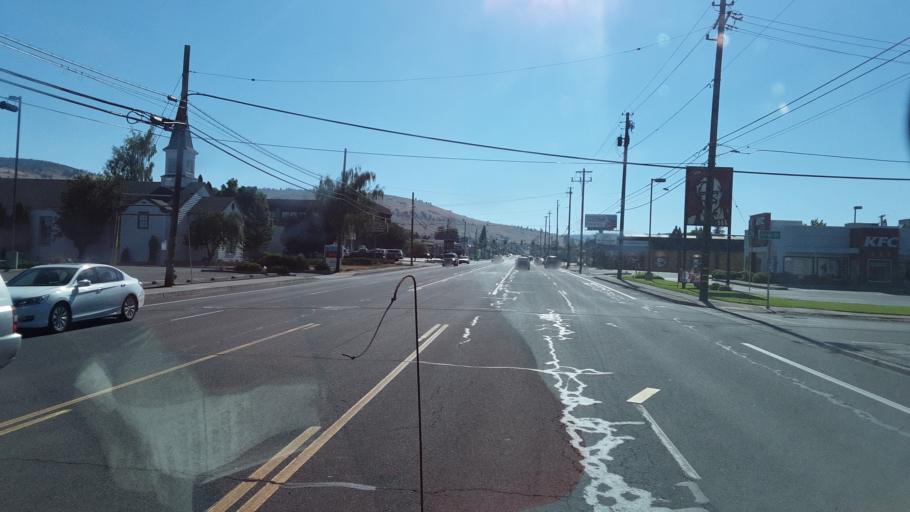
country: US
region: Oregon
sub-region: Klamath County
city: Altamont
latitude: 42.2064
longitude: -121.7353
